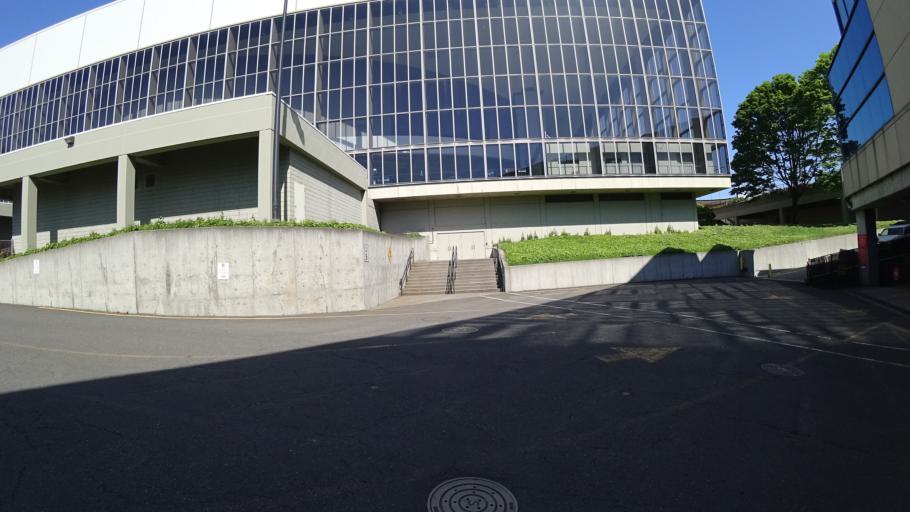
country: US
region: Oregon
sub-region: Multnomah County
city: Portland
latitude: 45.5317
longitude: -122.6684
